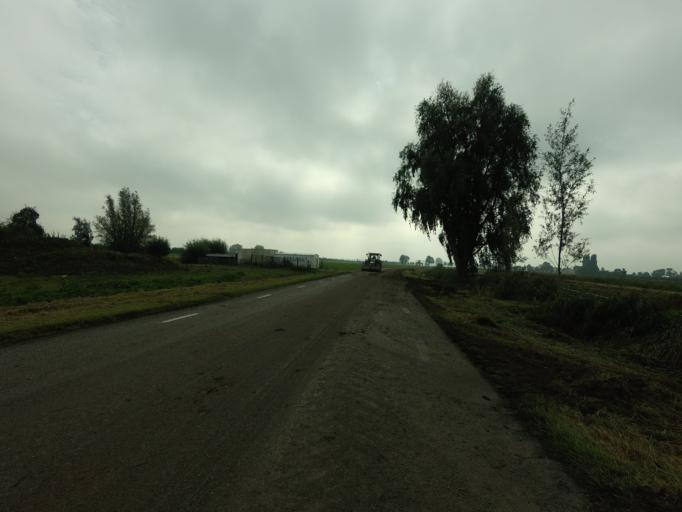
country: NL
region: Utrecht
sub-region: Gemeente Lopik
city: Lopik
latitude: 51.9388
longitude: 4.9075
